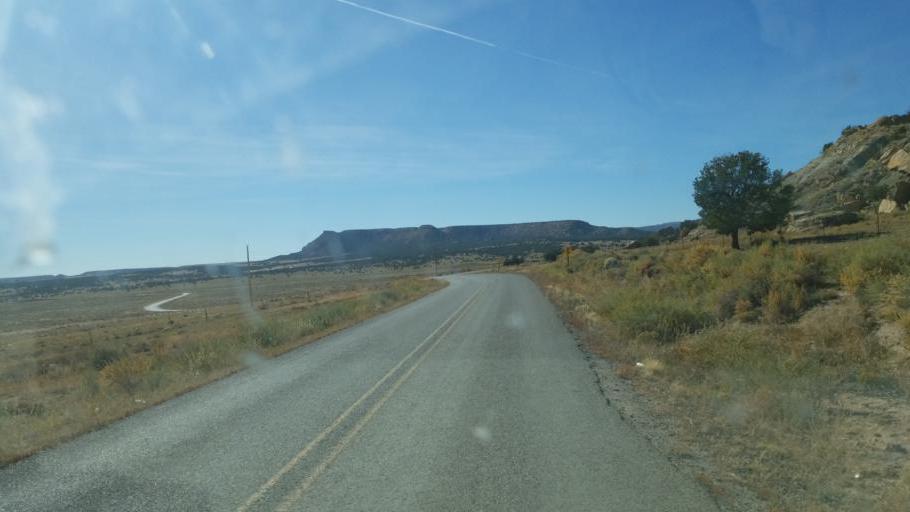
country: US
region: New Mexico
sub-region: McKinley County
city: Thoreau
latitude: 35.4792
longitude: -108.0451
